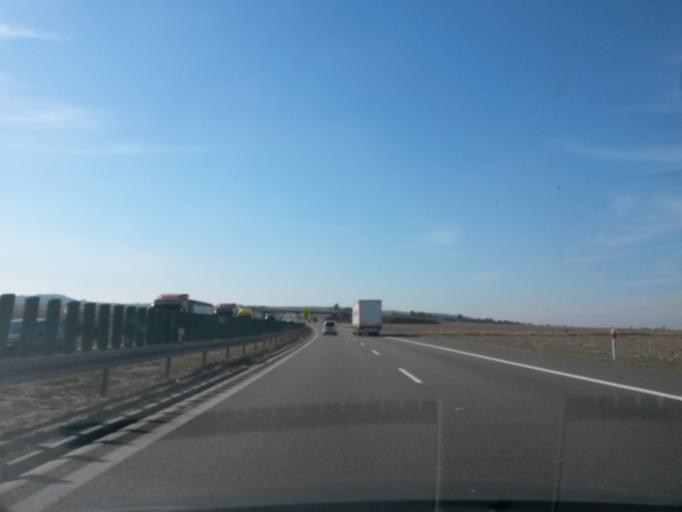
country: PL
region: Opole Voivodeship
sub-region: Powiat strzelecki
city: Lesnica
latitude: 50.4660
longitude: 18.2121
